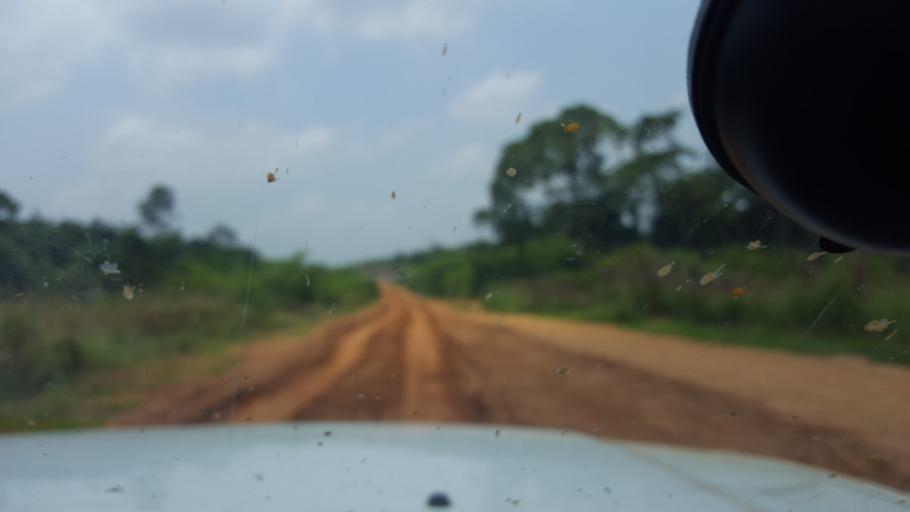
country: CD
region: Bandundu
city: Mushie
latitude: -3.7475
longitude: 16.6584
